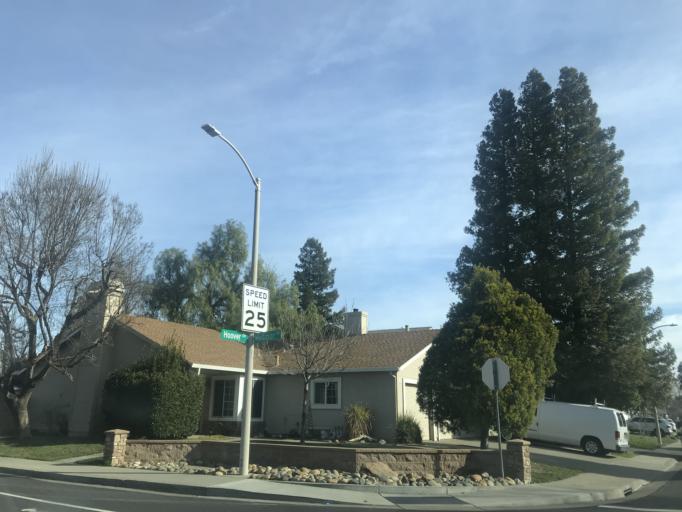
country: US
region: California
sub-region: Yolo County
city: Woodland
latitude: 38.6603
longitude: -121.7565
